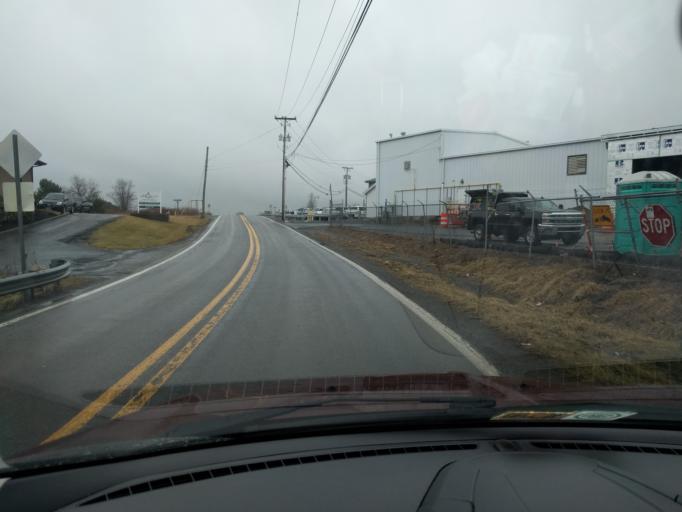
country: US
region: West Virginia
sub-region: Raleigh County
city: Mabscott
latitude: 37.7979
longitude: -81.2113
